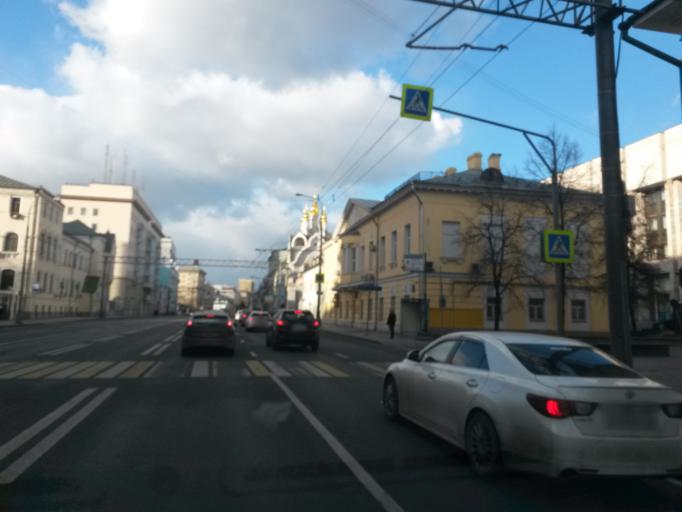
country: RU
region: Moscow
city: Moscow
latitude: 55.7757
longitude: 37.6324
